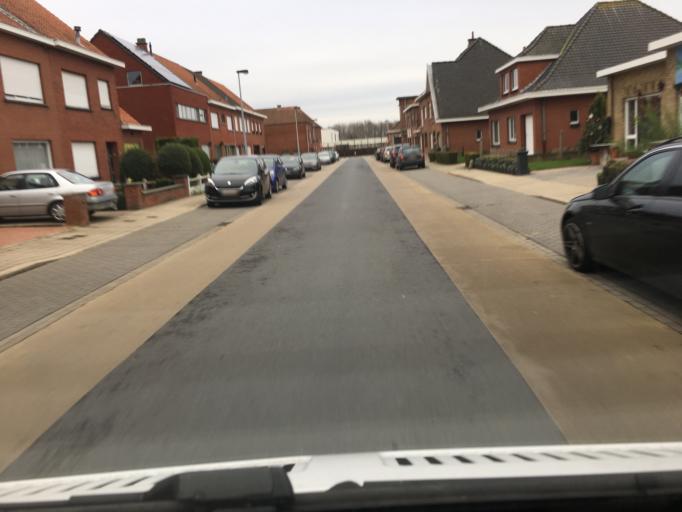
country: FR
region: Nord-Pas-de-Calais
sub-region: Departement du Nord
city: Wervicq-Sud
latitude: 50.7825
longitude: 3.0536
